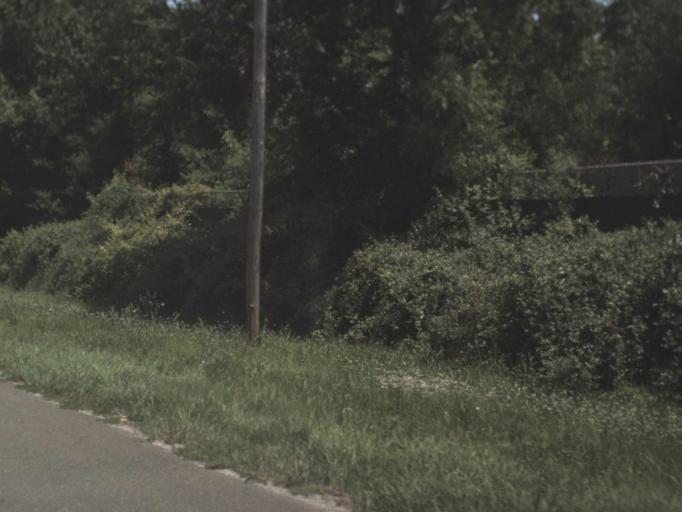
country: US
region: Florida
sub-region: Bradford County
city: Starke
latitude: 29.8988
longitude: -82.0880
